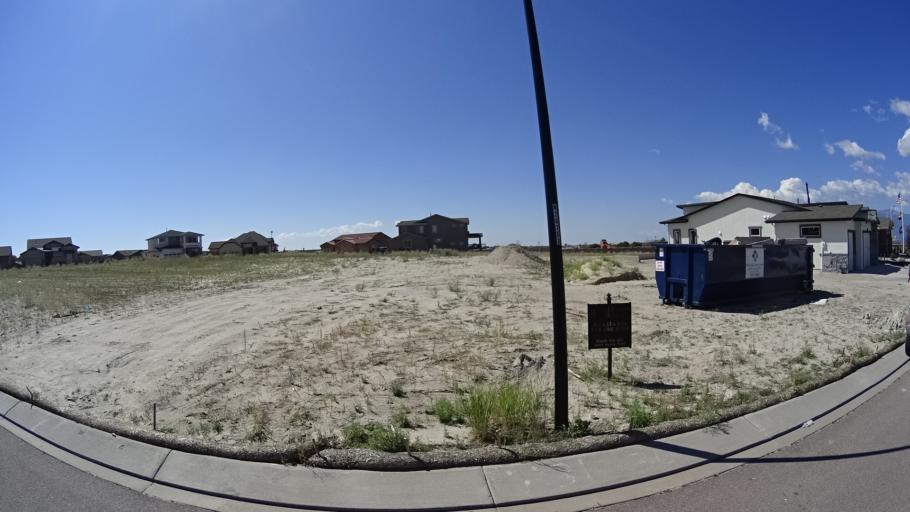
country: US
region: Colorado
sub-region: El Paso County
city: Black Forest
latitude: 38.9795
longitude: -104.7514
